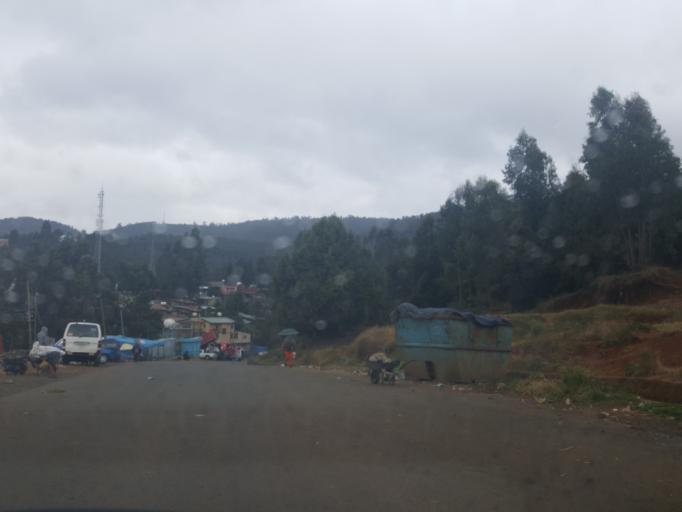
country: ET
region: Adis Abeba
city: Addis Ababa
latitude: 9.0695
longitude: 38.7395
